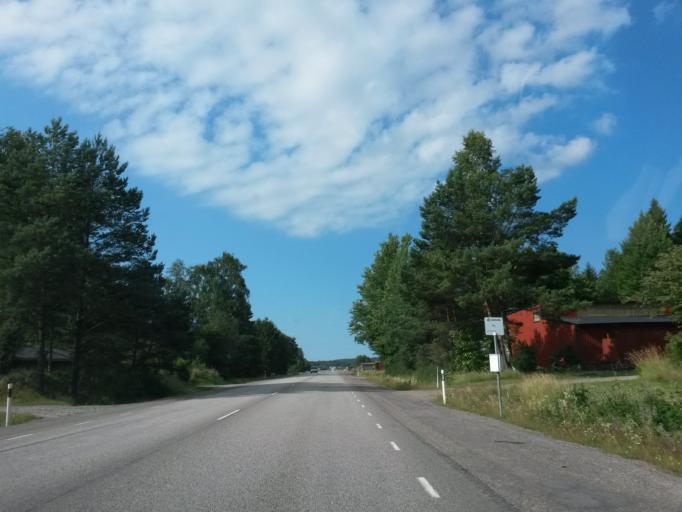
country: SE
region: Vaestra Goetaland
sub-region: Alingsas Kommun
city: Alingsas
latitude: 57.9841
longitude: 12.5980
